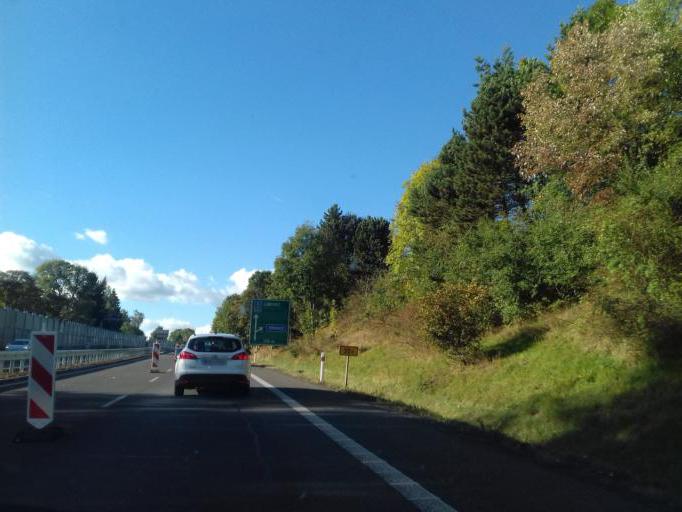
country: CZ
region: Liberecky
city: Hodkovice nad Mohelkou
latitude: 50.6960
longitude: 15.1023
